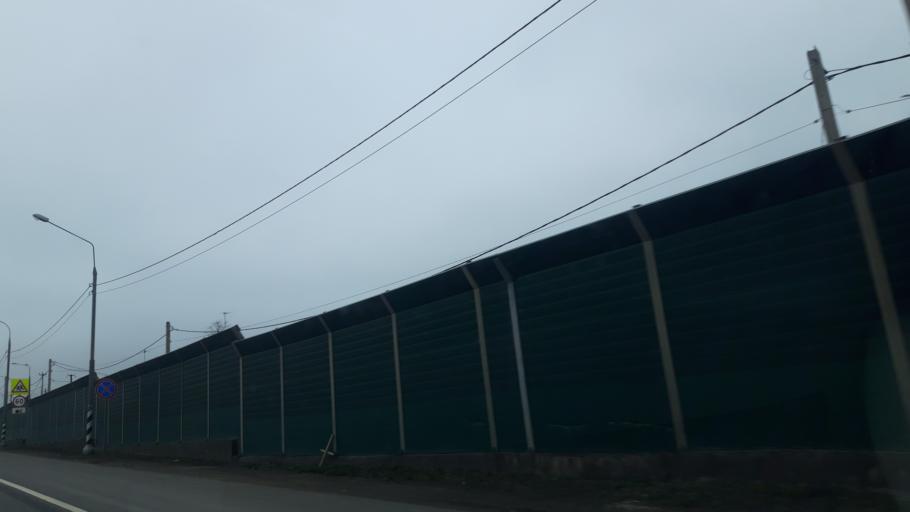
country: RU
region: Moskovskaya
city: Lozhki
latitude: 56.0907
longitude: 37.1118
